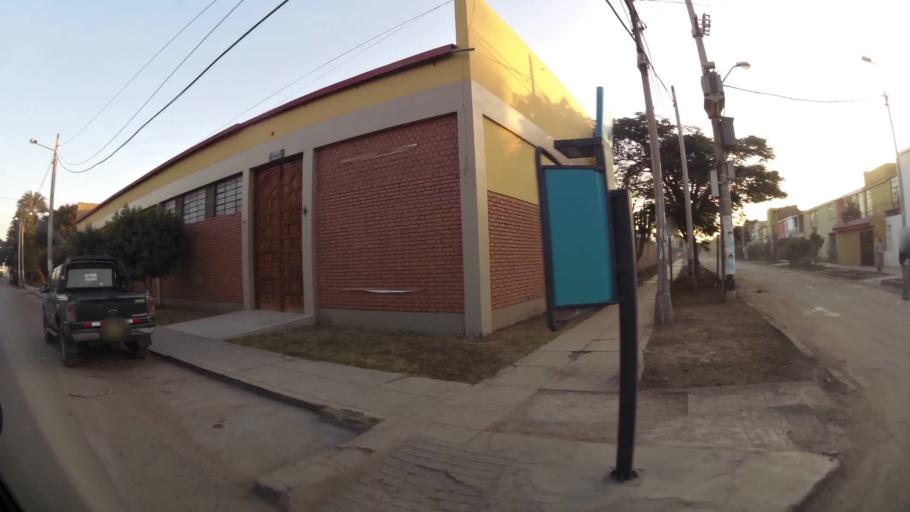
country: PE
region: Ica
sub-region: Provincia de Ica
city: Ica
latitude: -14.0759
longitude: -75.7280
